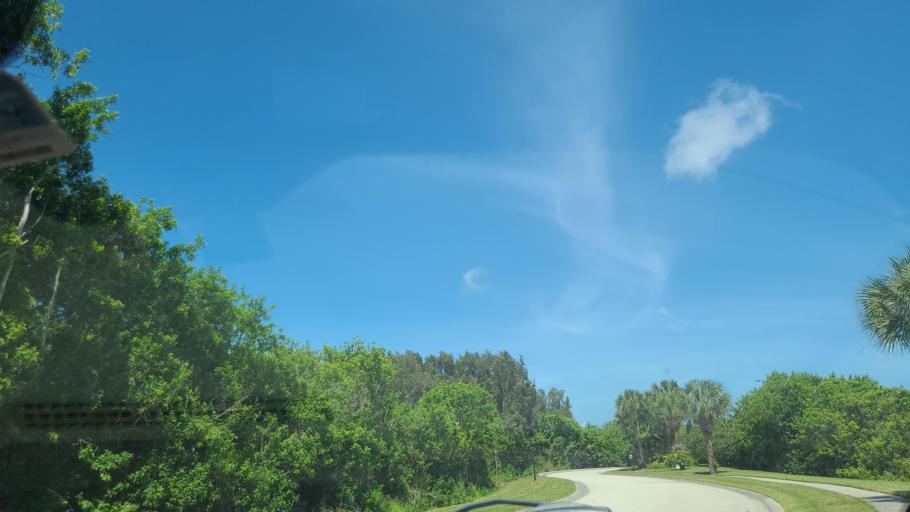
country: US
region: Florida
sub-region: Indian River County
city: Sebastian
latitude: 27.7890
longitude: -80.4650
